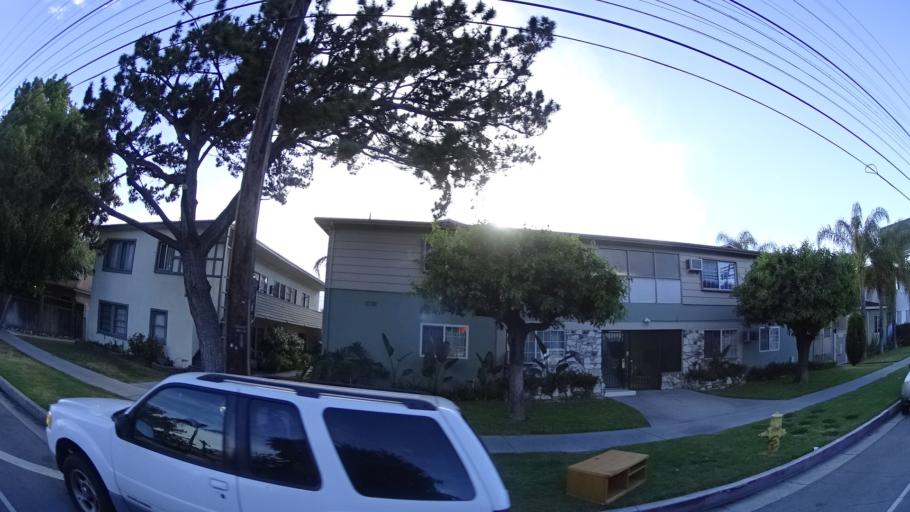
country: US
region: California
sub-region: Los Angeles County
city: North Hollywood
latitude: 34.1642
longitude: -118.3616
